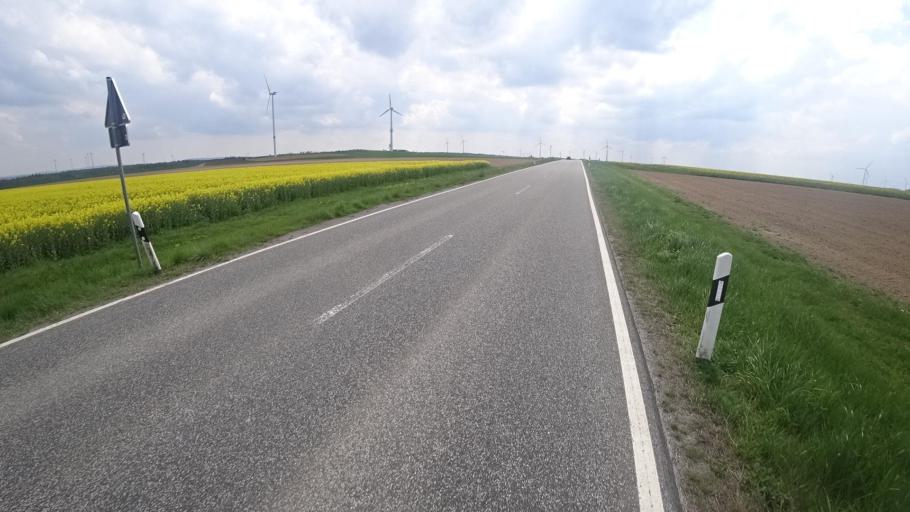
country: DE
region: Rheinland-Pfalz
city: Braunshorn
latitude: 50.0665
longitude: 7.5135
